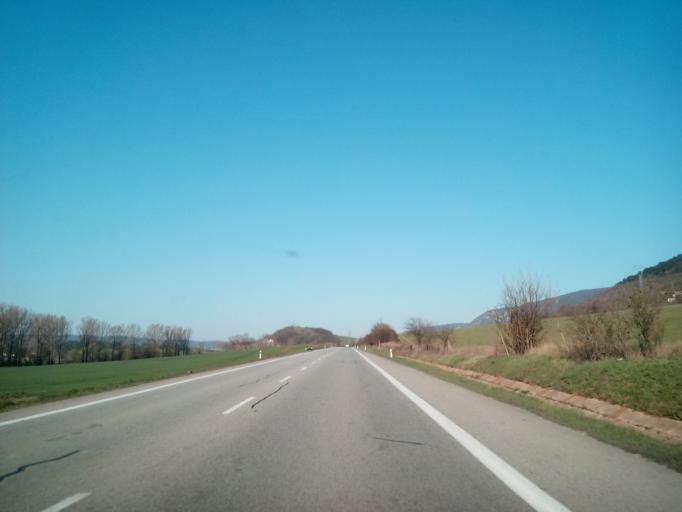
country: SK
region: Kosicky
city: Medzev
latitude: 48.6103
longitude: 20.8582
